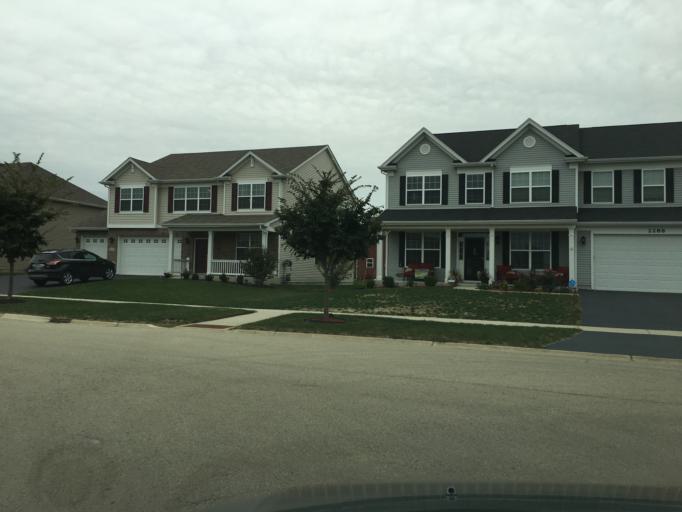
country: US
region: Illinois
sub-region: Will County
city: Plainfield
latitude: 41.6549
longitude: -88.1726
